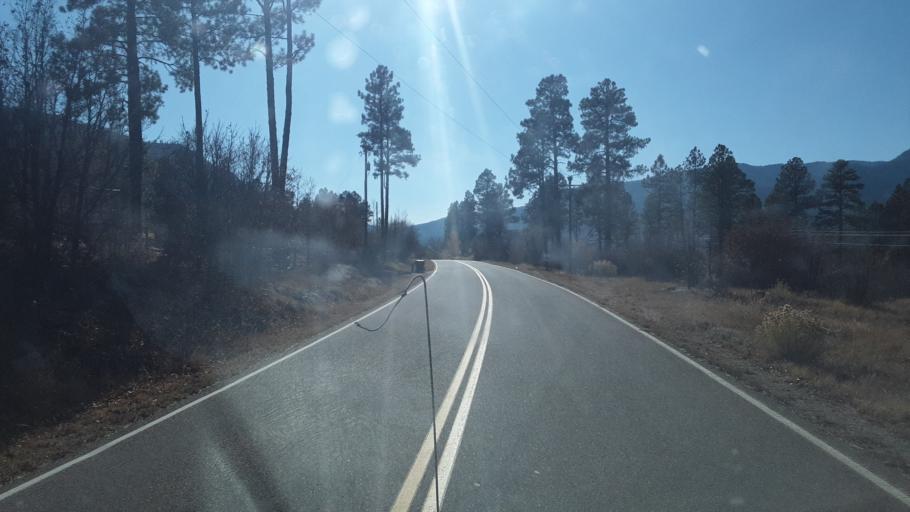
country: US
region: Colorado
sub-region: La Plata County
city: Durango
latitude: 37.4118
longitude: -107.8114
